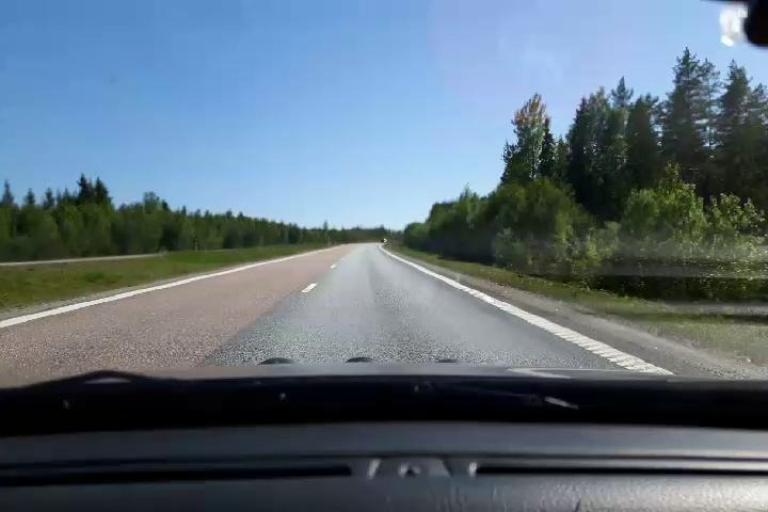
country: SE
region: Gaevleborg
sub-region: Soderhamns Kommun
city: Soderhamn
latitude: 61.4731
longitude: 16.9897
